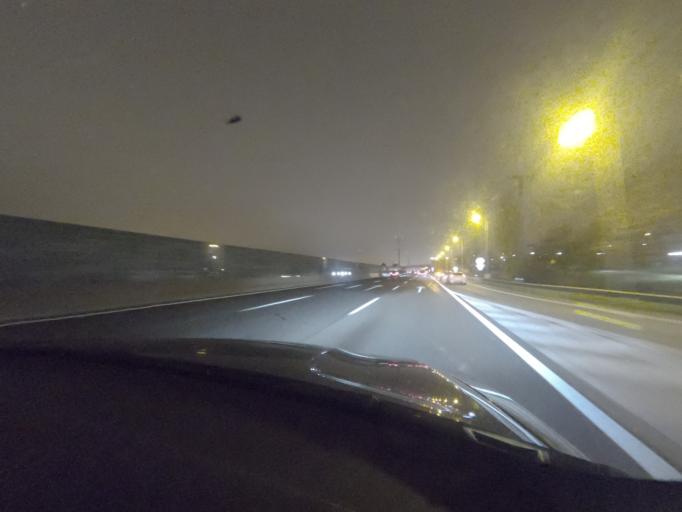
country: PT
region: Lisbon
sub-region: Loures
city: Sao Joao da Talha
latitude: 38.8226
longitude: -9.0995
